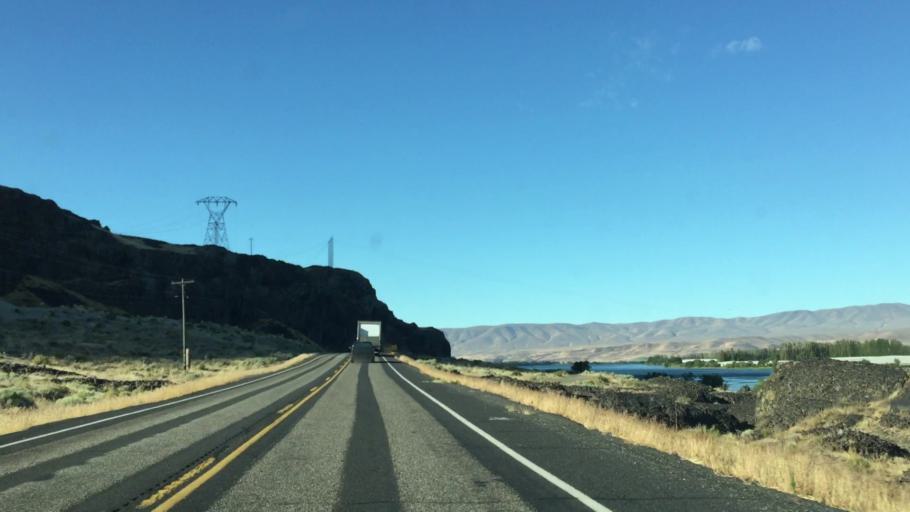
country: US
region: Washington
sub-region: Grant County
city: Mattawa
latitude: 46.8050
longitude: -119.9222
